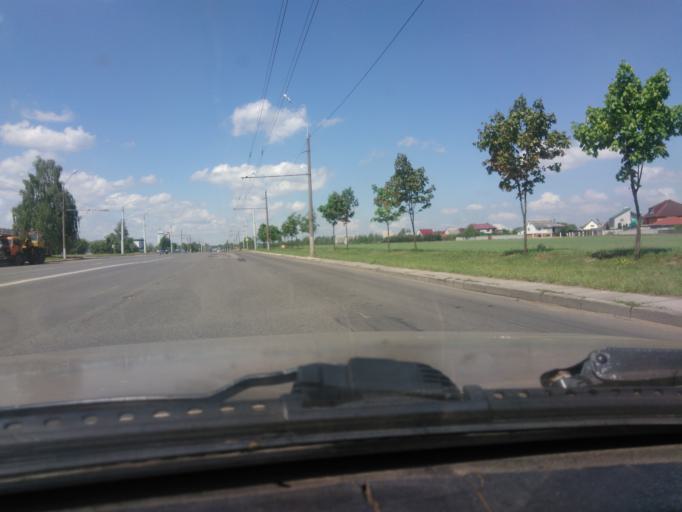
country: BY
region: Mogilev
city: Palykavichy Pyershyya
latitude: 53.9617
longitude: 30.3585
